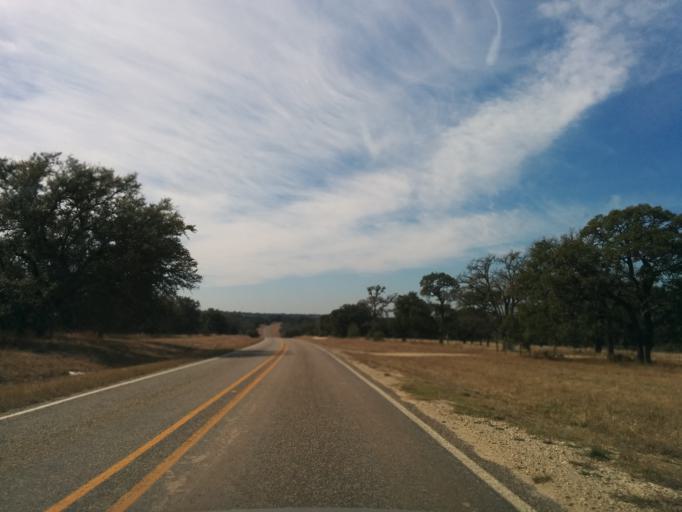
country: US
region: Texas
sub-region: Blanco County
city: Blanco
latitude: 29.9640
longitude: -98.5341
